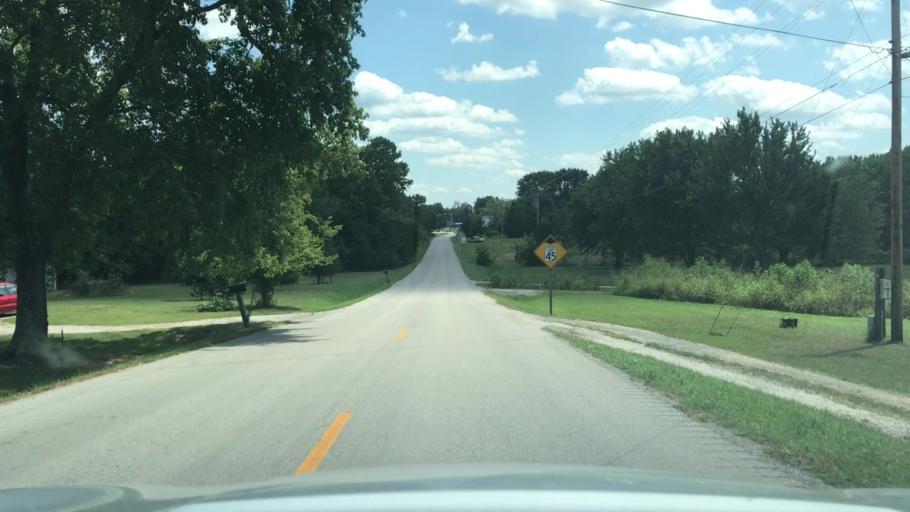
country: US
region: Kentucky
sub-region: Christian County
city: Hopkinsville
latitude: 36.9886
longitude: -87.3606
